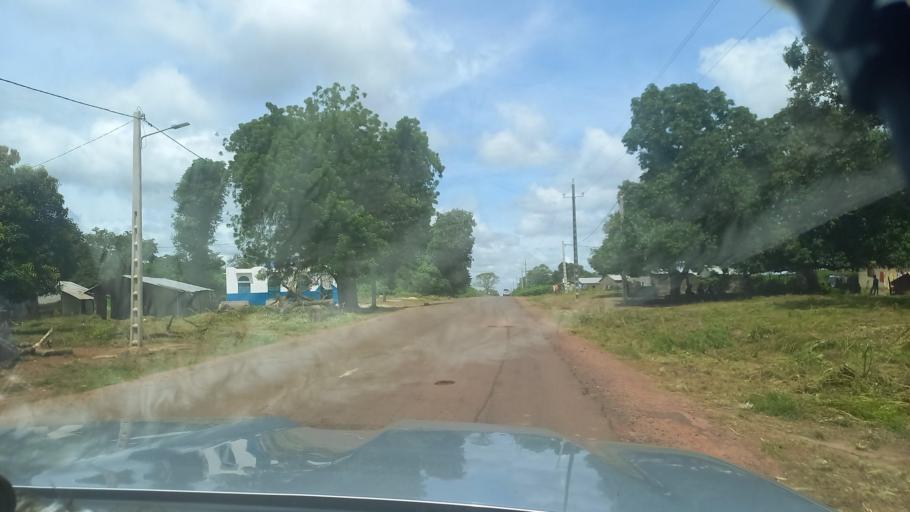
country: GM
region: Lower River
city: Kaiaf
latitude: 13.2210
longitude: -15.5412
